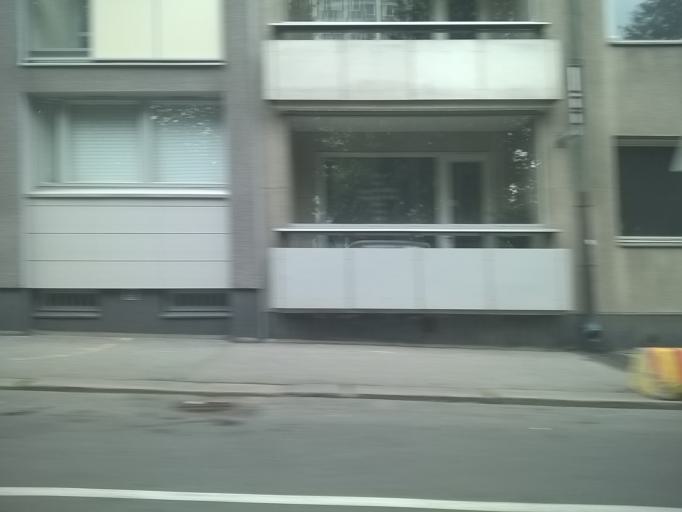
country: FI
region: Pirkanmaa
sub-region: Tampere
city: Tampere
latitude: 61.5004
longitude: 23.7512
